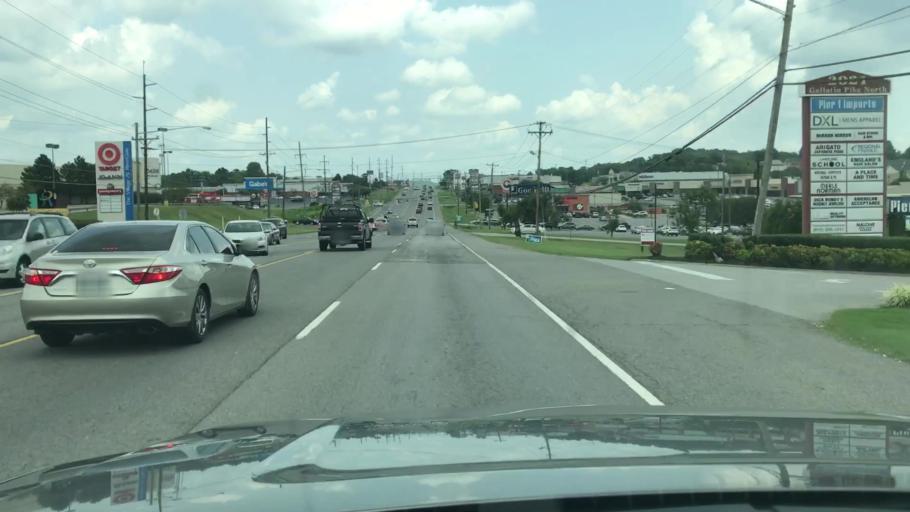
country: US
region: Tennessee
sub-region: Davidson County
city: Goodlettsville
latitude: 36.3015
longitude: -86.6936
